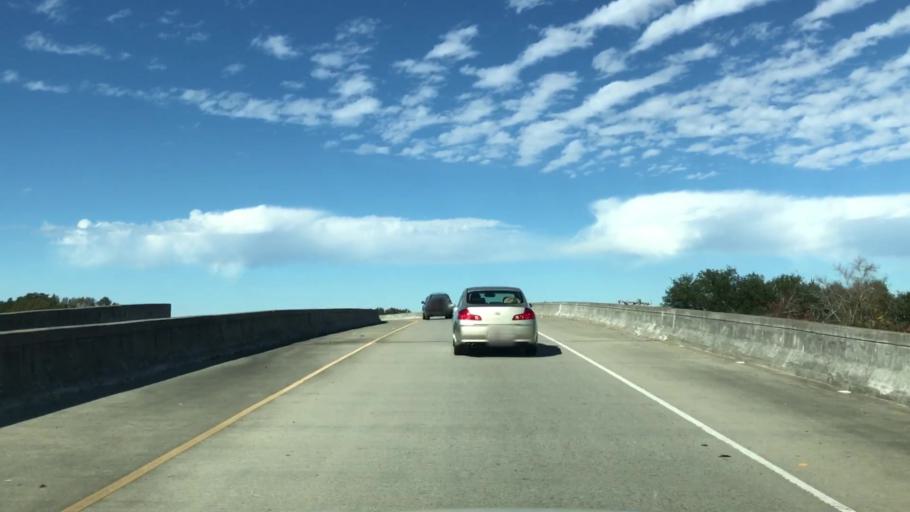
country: US
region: South Carolina
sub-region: Charleston County
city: Charleston
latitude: 32.7794
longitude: -79.9684
